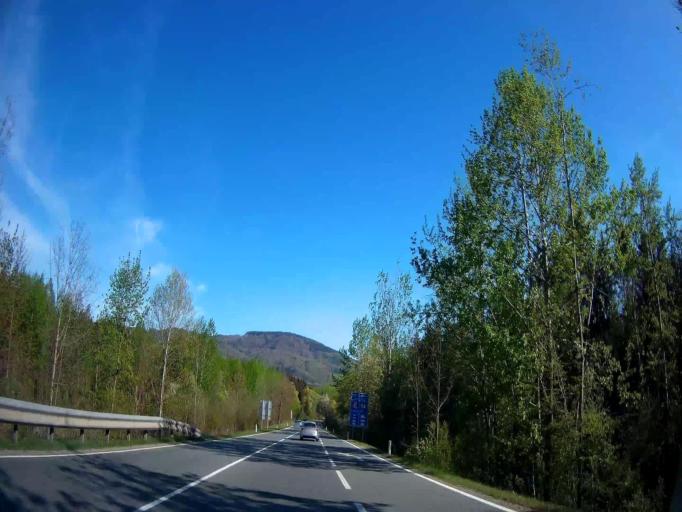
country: AT
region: Salzburg
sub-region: Politischer Bezirk Salzburg-Umgebung
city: Oberndorf bei Salzburg
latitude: 47.9323
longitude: 12.9646
